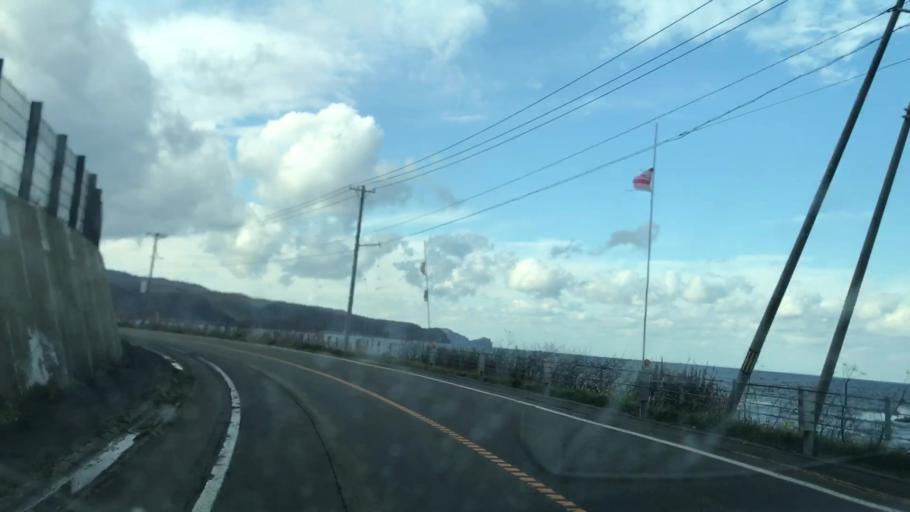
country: JP
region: Hokkaido
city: Yoichi
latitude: 43.3381
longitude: 140.4500
